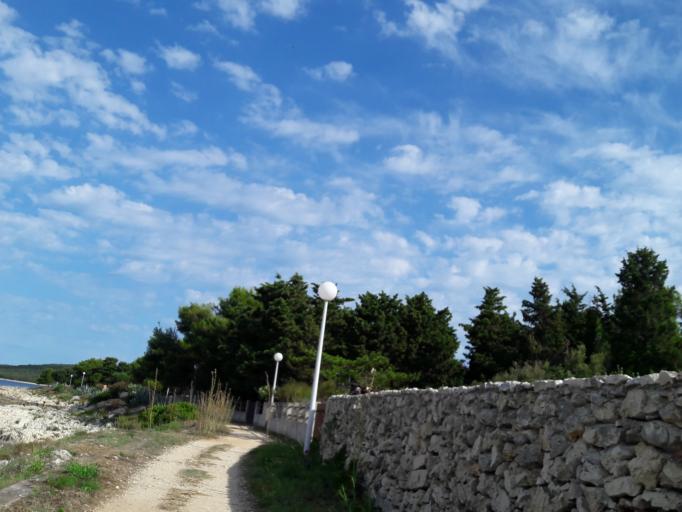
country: HR
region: Licko-Senjska
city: Novalja
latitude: 44.3787
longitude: 14.6900
